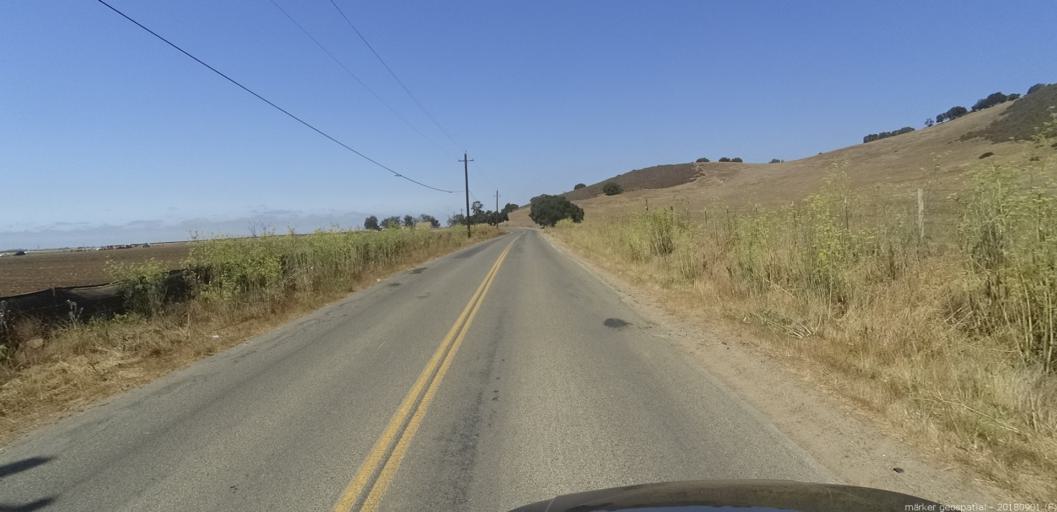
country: US
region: California
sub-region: Monterey County
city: Salinas
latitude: 36.6868
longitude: -121.5643
